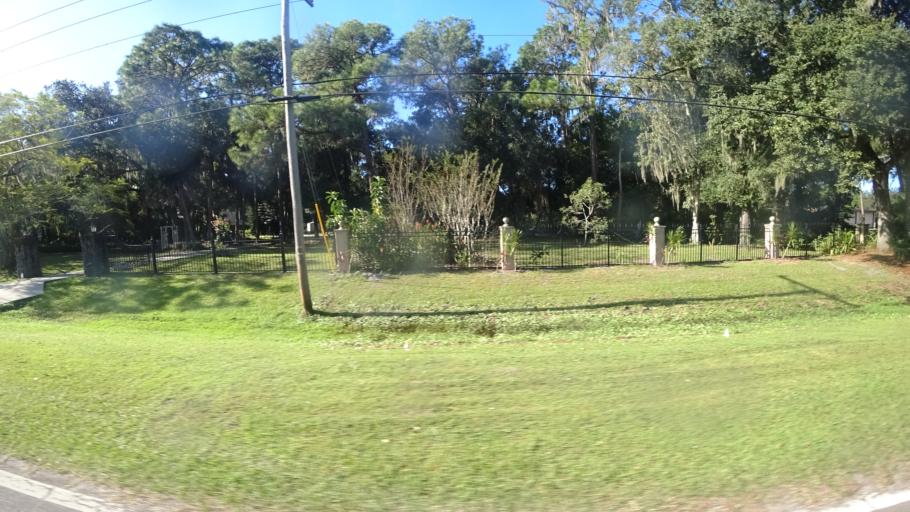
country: US
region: Florida
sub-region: Hillsborough County
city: Ruskin
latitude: 27.6486
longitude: -82.4200
